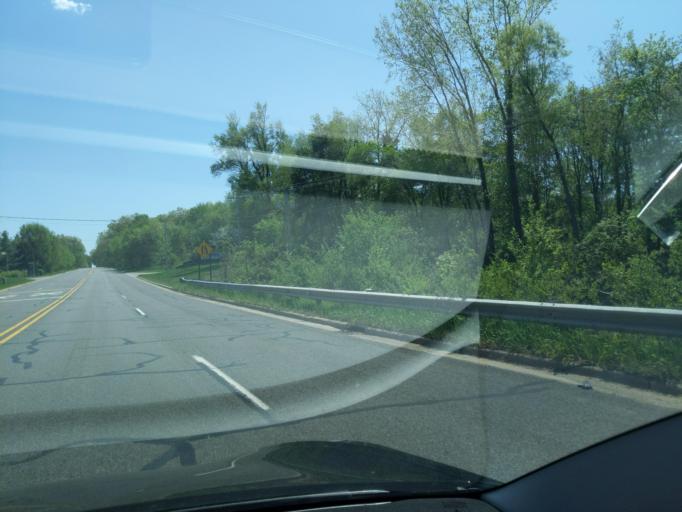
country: US
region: Michigan
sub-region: Kent County
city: Forest Hills
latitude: 42.9584
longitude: -85.5403
